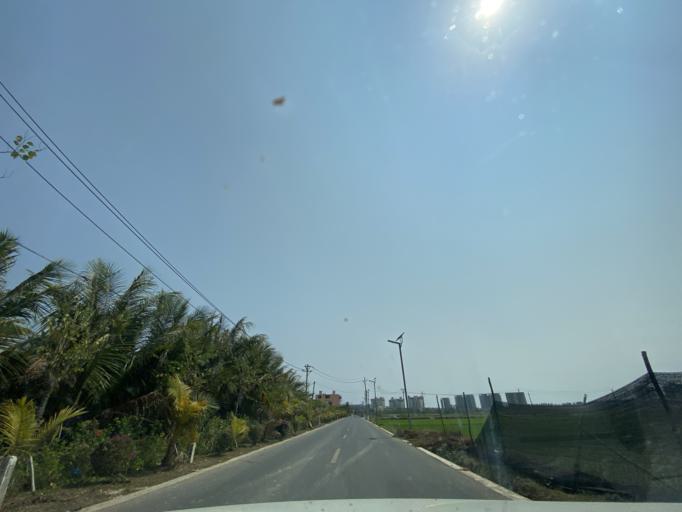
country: CN
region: Hainan
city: Yingzhou
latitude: 18.4126
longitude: 109.8152
